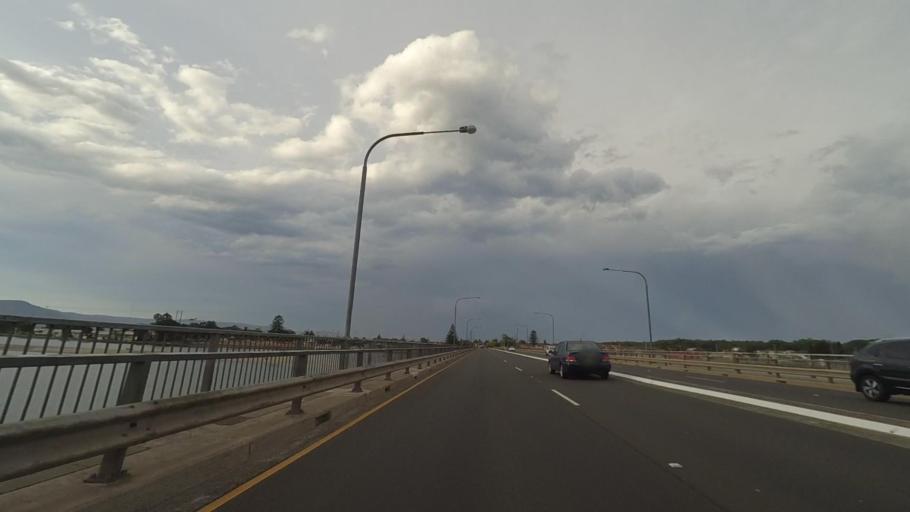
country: AU
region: New South Wales
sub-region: Shellharbour
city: Lake Illawarra
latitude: -34.5370
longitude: 150.8665
